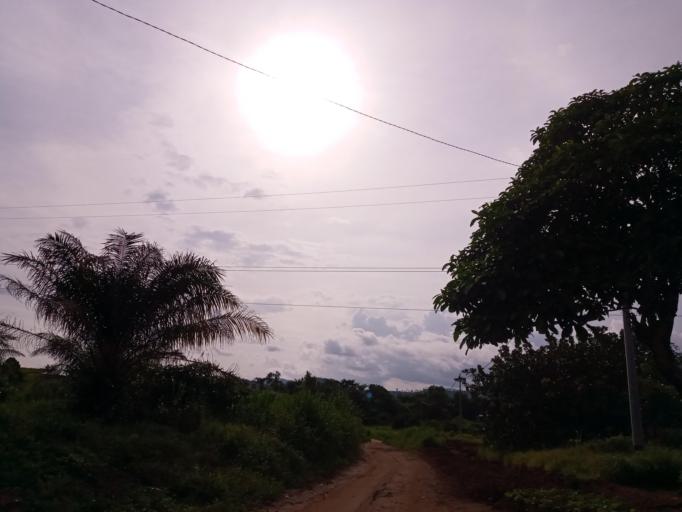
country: SL
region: Northern Province
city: Bumbuna
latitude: 9.0451
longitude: -11.7567
